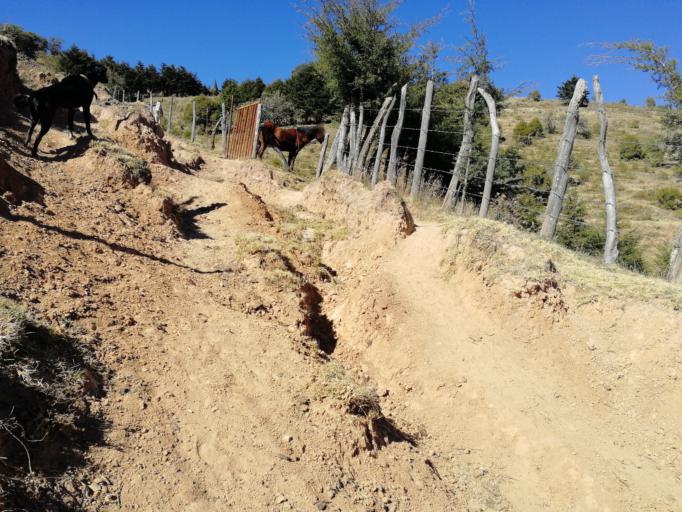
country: MX
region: San Luis Potosi
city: Zaragoza
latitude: 22.0063
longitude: -100.6099
